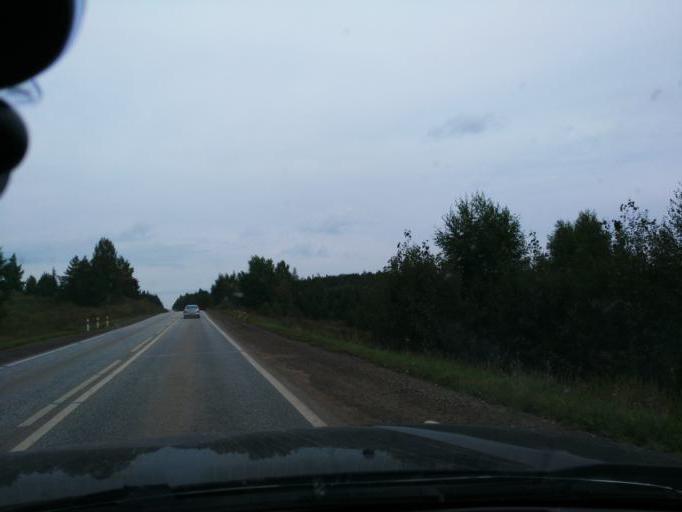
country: RU
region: Perm
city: Chernushka
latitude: 56.5769
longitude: 56.1350
